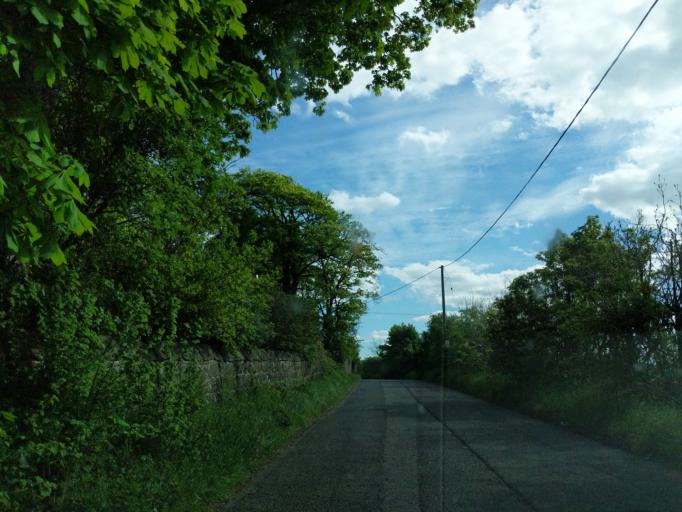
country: GB
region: Scotland
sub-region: Edinburgh
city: Ratho
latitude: 55.9352
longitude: -3.3511
